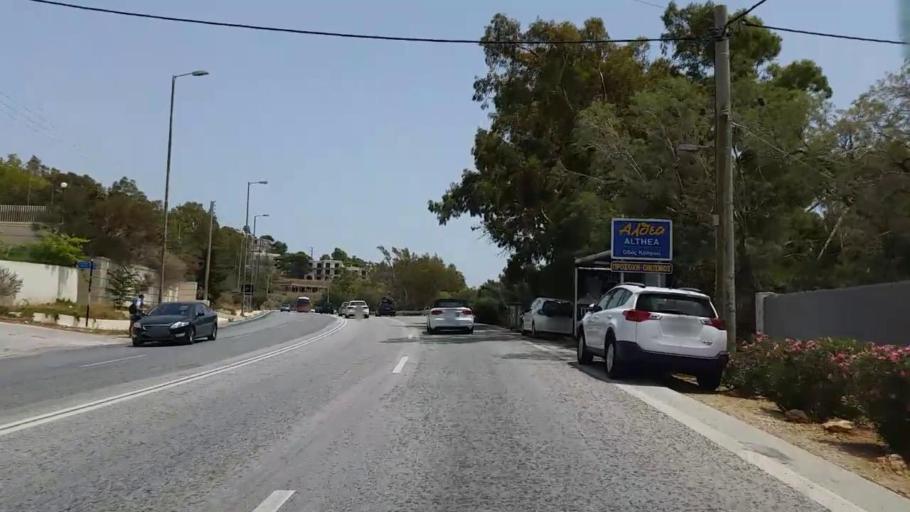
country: GR
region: Attica
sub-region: Nomarchia Anatolikis Attikis
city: Agios Dimitrios Kropias
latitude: 37.8072
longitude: 23.8501
